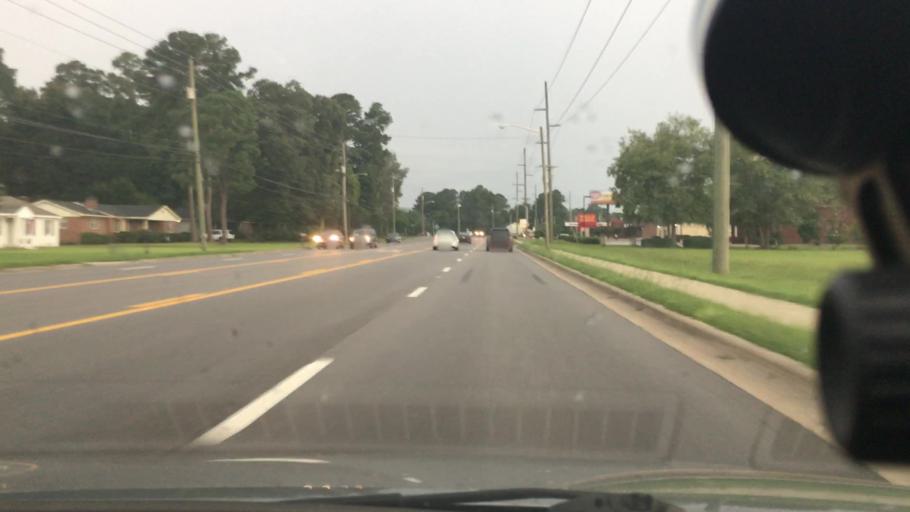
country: US
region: North Carolina
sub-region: Pitt County
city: Greenville
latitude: 35.5923
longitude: -77.3429
